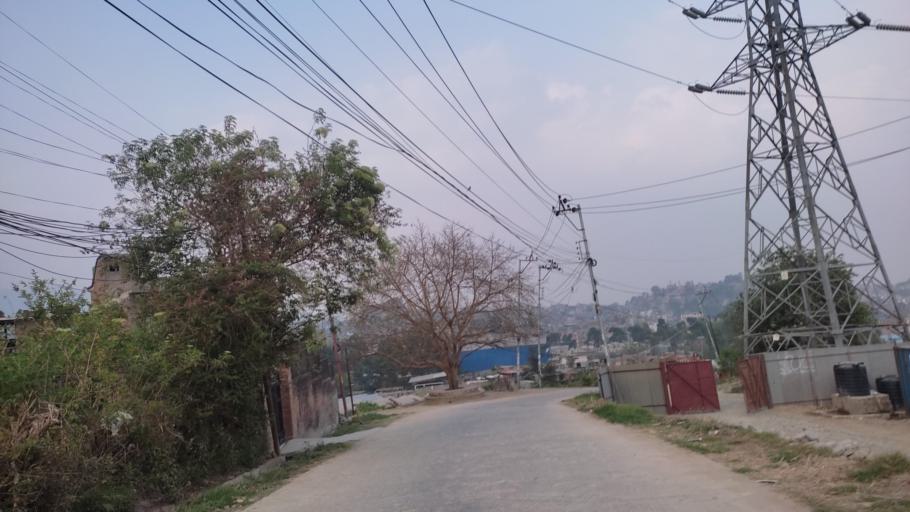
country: NP
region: Central Region
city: Kirtipur
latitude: 27.6790
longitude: 85.2514
